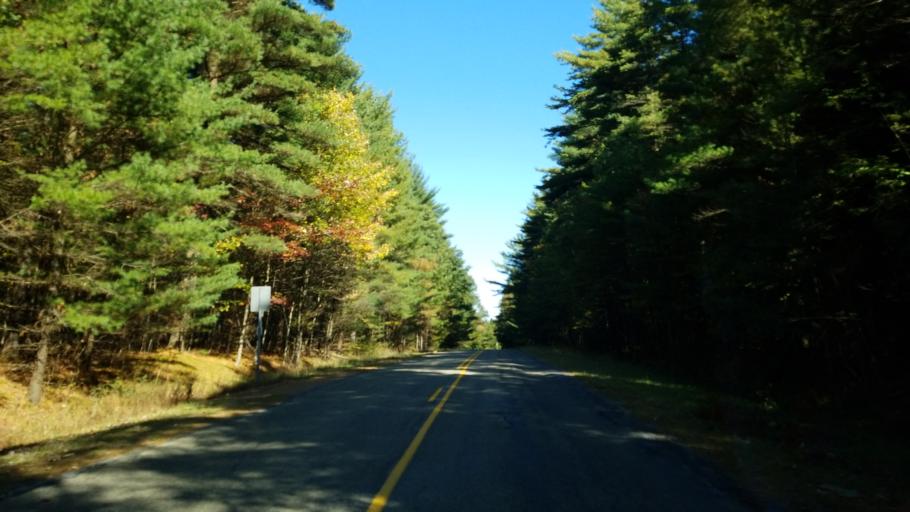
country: US
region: Pennsylvania
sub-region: Clearfield County
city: Shiloh
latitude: 41.2607
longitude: -78.3037
